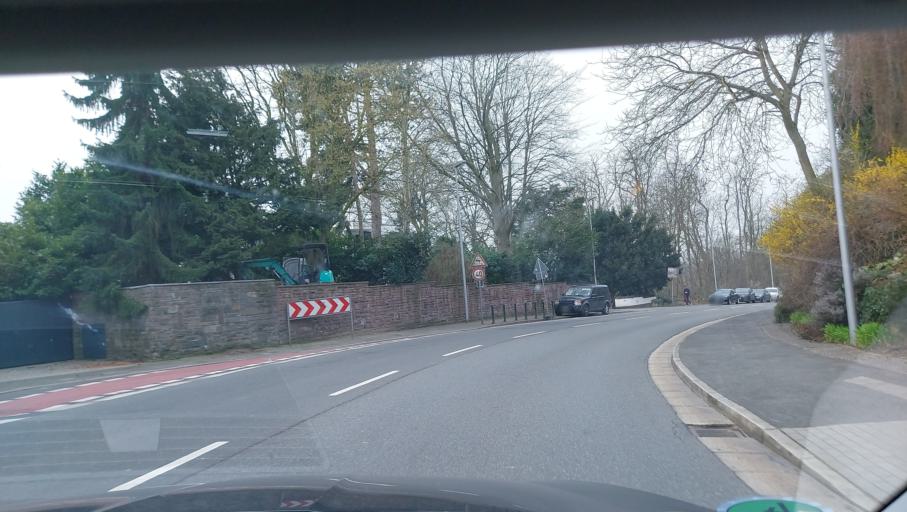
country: DE
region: North Rhine-Westphalia
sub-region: Regierungsbezirk Dusseldorf
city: Erkrath
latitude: 51.2469
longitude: 6.8630
